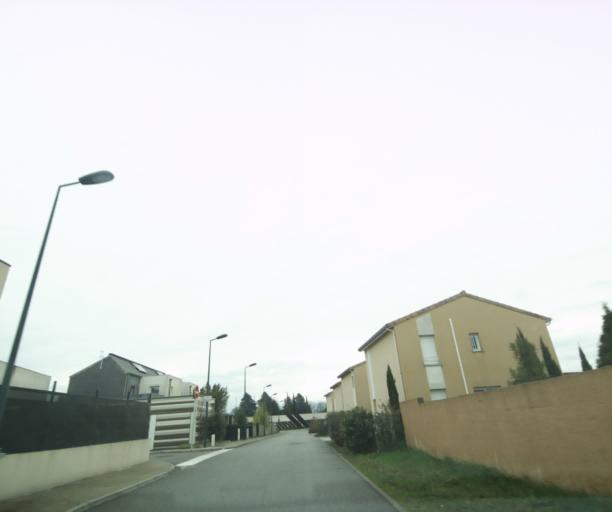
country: FR
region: Rhone-Alpes
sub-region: Departement de la Drome
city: Bourg-les-Valence
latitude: 44.9554
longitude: 4.8865
